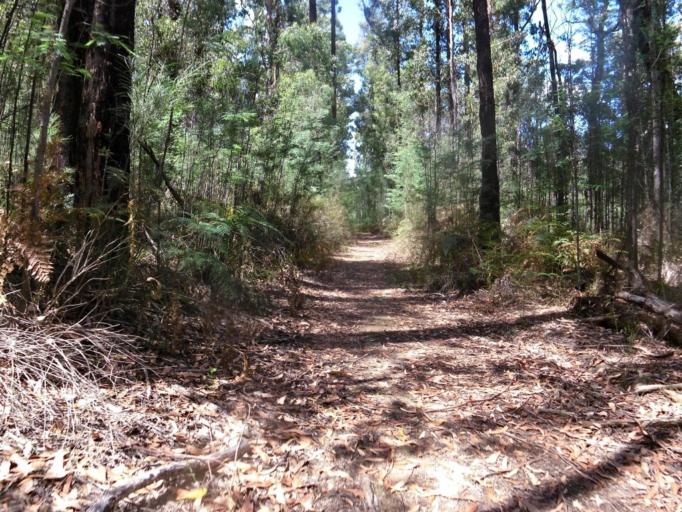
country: AU
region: Victoria
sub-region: Yarra Ranges
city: Healesville
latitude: -37.4206
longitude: 145.5664
